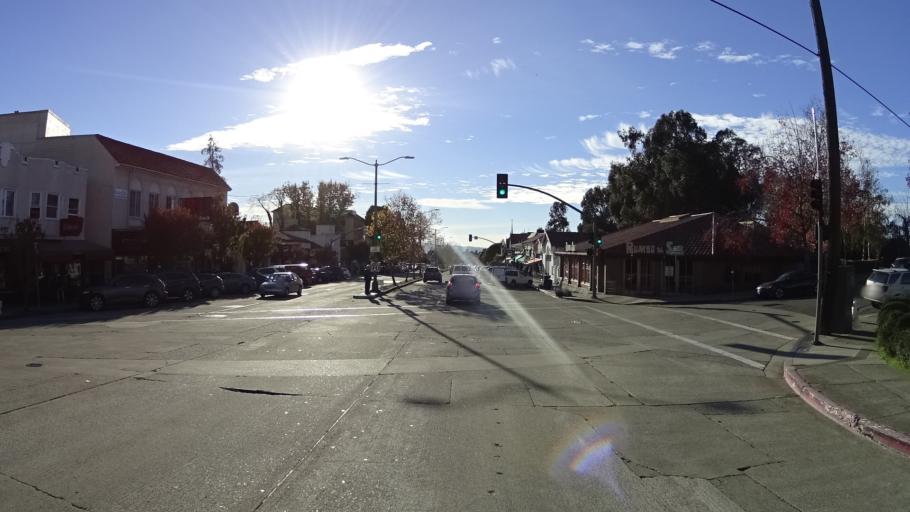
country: US
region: California
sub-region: Alameda County
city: Piedmont
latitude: 37.8078
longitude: -122.2215
